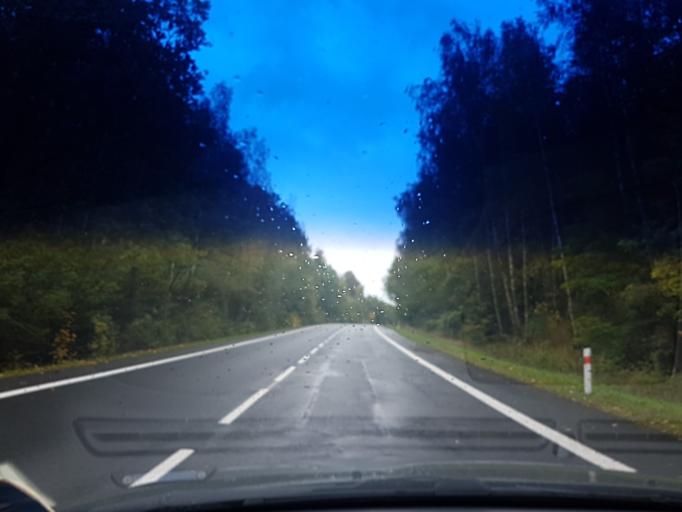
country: CZ
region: Karlovarsky
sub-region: Okres Cheb
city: Cheb
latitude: 50.0803
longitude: 12.3378
